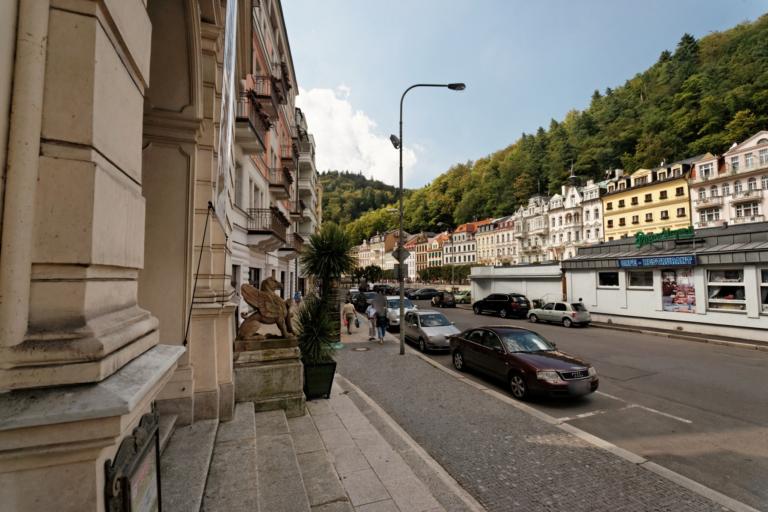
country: CZ
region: Karlovarsky
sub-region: Okres Karlovy Vary
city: Karlovy Vary
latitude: 50.2211
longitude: 12.8815
